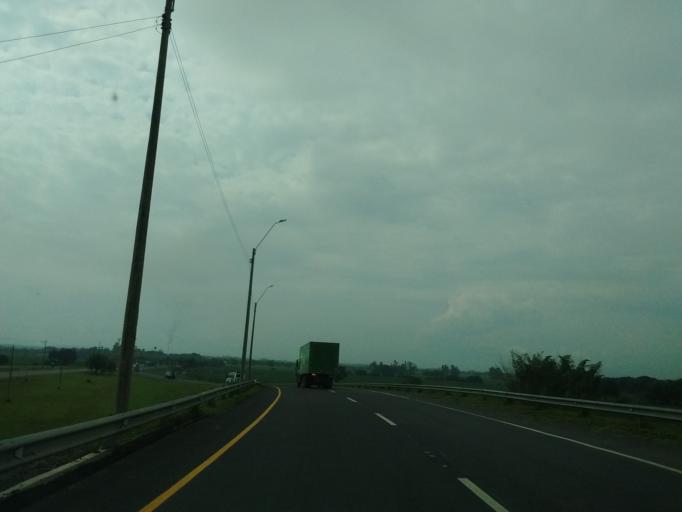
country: CO
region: Cauca
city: Puerto Tejada
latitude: 3.1579
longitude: -76.4600
